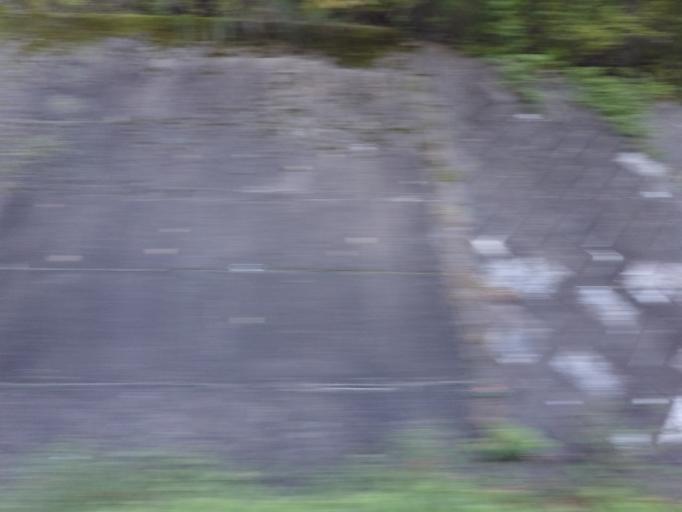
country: JP
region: Nagano
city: Shiojiri
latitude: 36.0032
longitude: 137.7701
